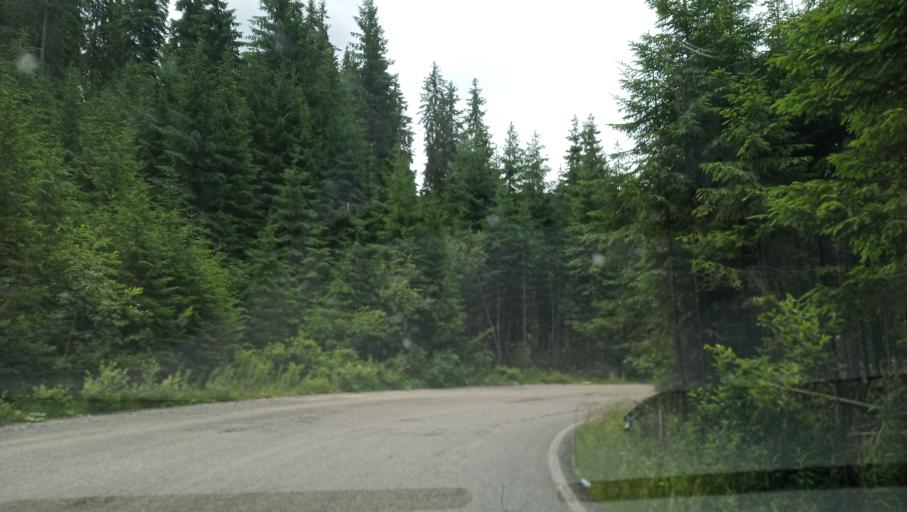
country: RO
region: Valcea
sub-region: Comuna Voineasa
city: Voineasa
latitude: 45.4160
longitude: 23.7195
